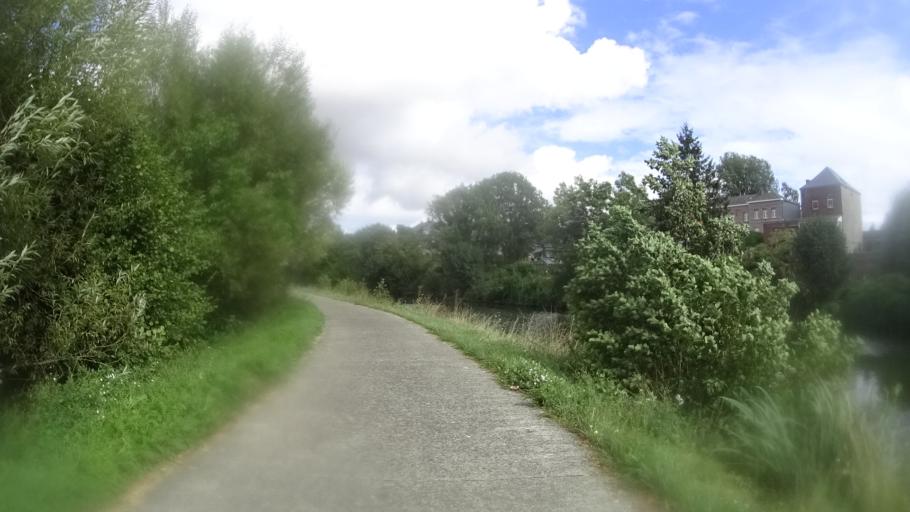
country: BE
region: Wallonia
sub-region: Province du Hainaut
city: Merbes-le-Chateau
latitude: 50.3085
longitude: 4.1471
